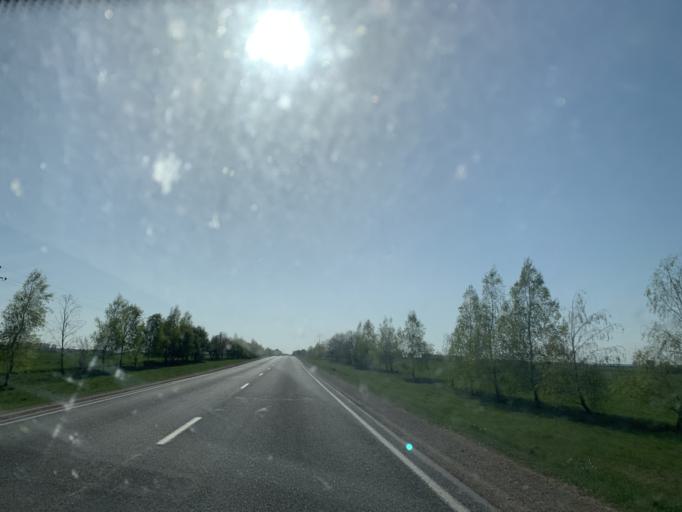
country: BY
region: Minsk
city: Kapyl'
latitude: 53.2555
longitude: 26.9266
